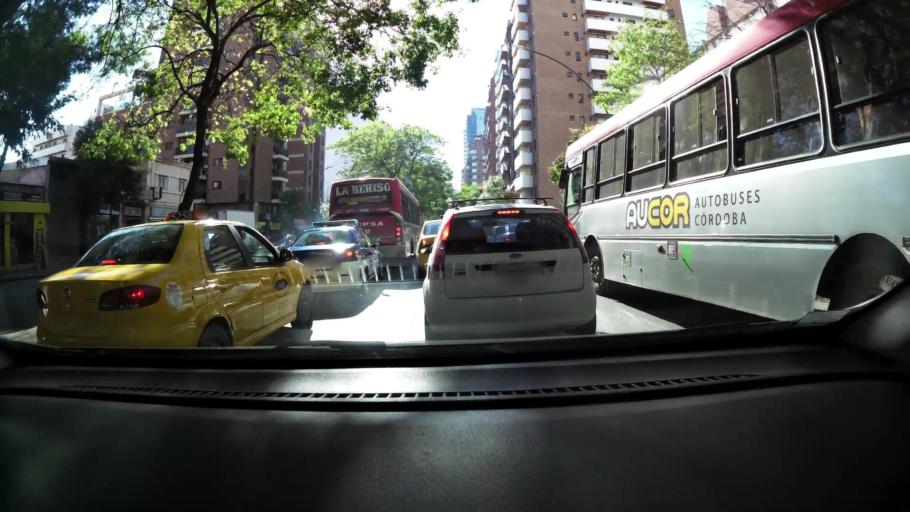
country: AR
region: Cordoba
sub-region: Departamento de Capital
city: Cordoba
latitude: -31.4224
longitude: -64.1796
